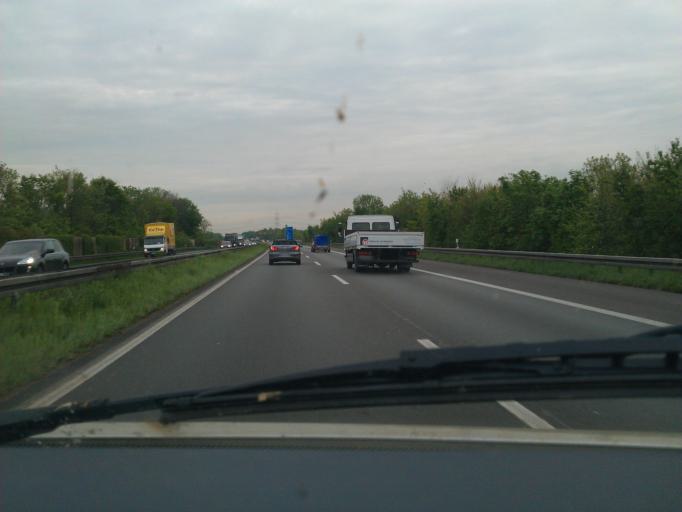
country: DE
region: North Rhine-Westphalia
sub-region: Regierungsbezirk Dusseldorf
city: Moers
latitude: 51.4151
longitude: 6.6055
